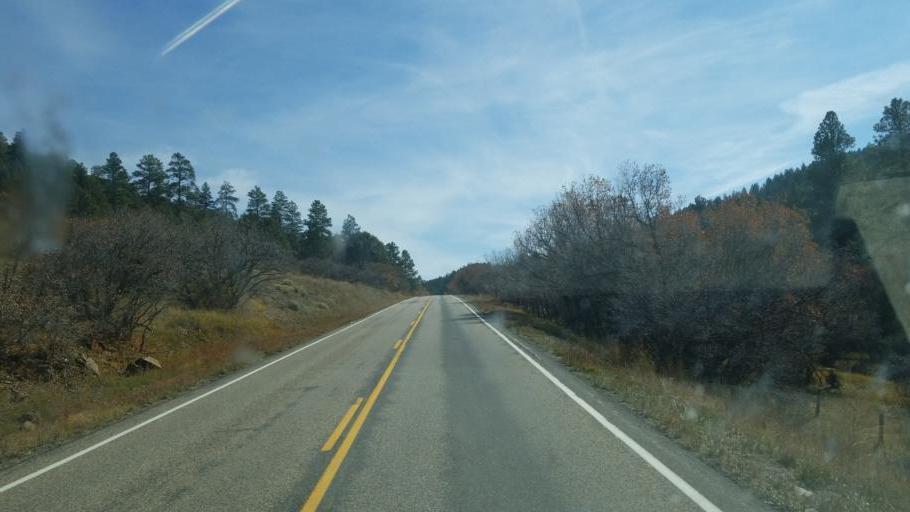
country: US
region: New Mexico
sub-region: Rio Arriba County
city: Dulce
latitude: 37.0788
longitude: -106.8577
